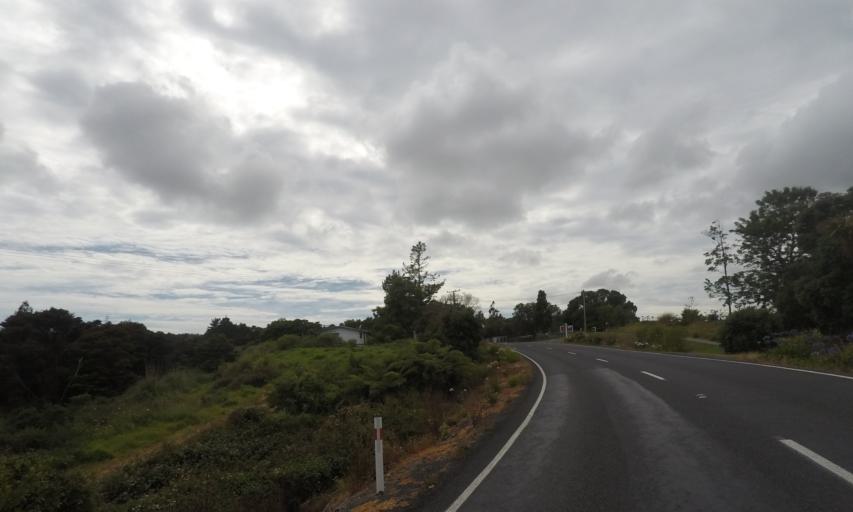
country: NZ
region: Northland
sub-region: Whangarei
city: Ruakaka
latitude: -35.7695
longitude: 174.4781
